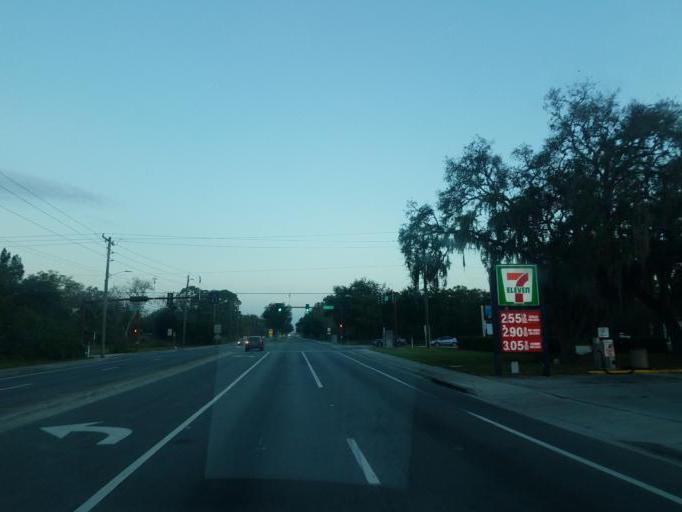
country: US
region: Florida
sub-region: Sarasota County
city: North Sarasota
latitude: 27.3811
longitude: -82.5056
